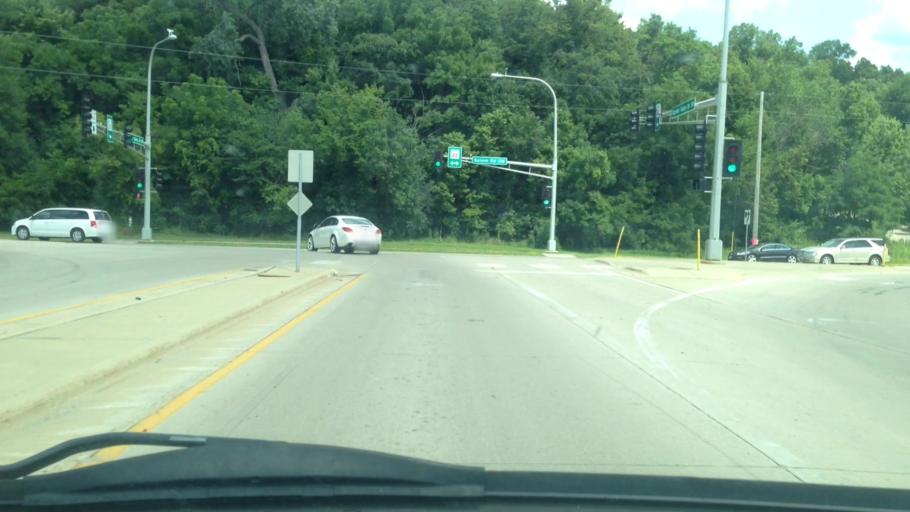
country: US
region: Minnesota
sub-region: Olmsted County
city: Rochester
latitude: 43.9982
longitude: -92.4979
